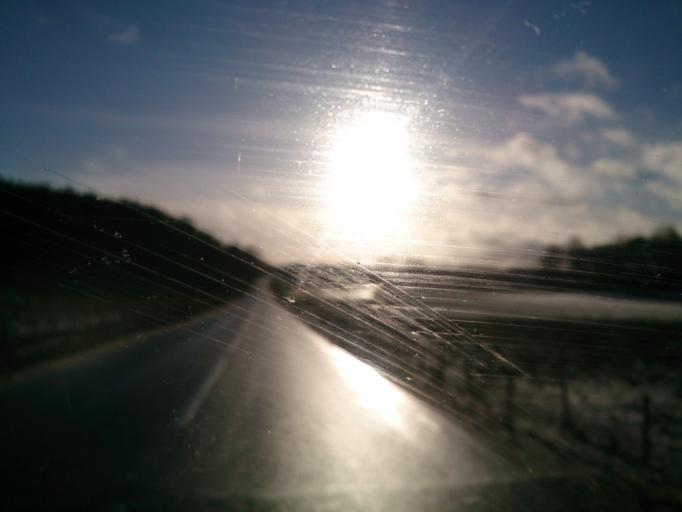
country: SE
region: OEstergoetland
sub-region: Atvidabergs Kommun
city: Atvidaberg
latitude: 58.2997
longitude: 15.8891
